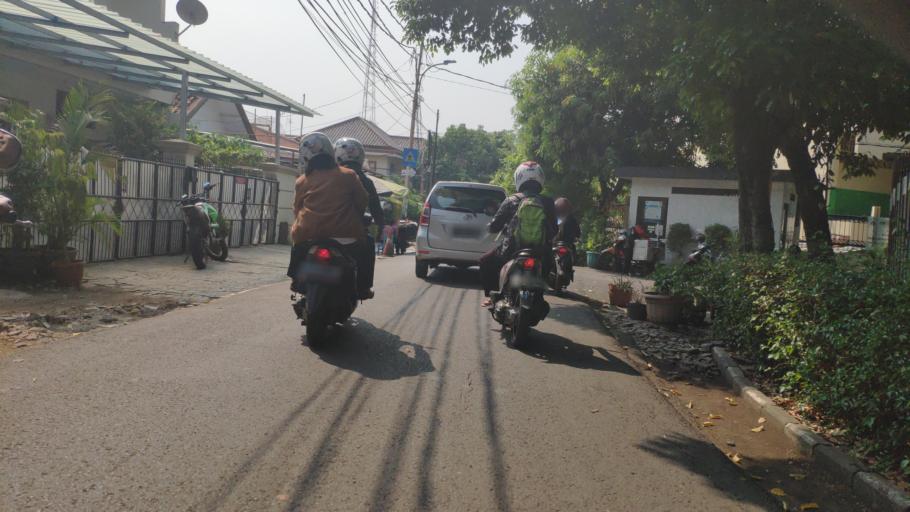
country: ID
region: Jakarta Raya
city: Jakarta
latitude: -6.2530
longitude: 106.7956
